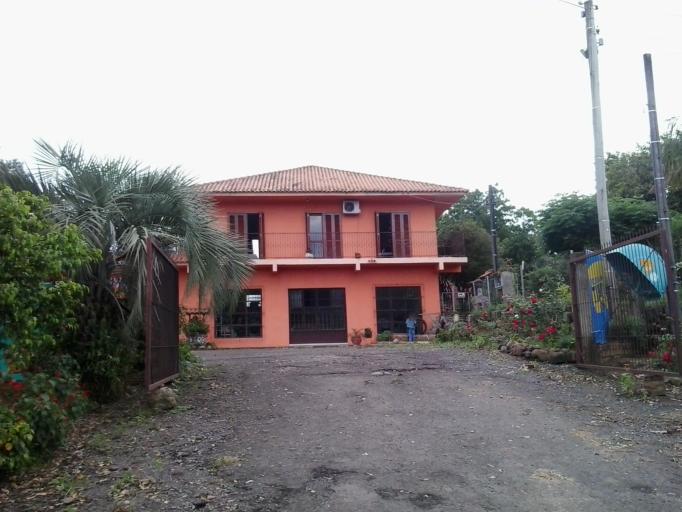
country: BR
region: Rio Grande do Sul
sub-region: Santa Maria
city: Santa Maria
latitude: -29.7326
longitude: -53.5386
